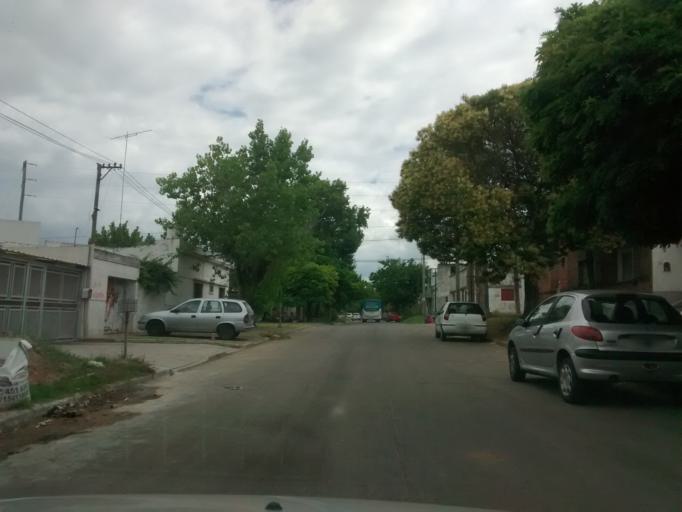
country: AR
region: Buenos Aires
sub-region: Partido de La Plata
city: La Plata
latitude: -34.9352
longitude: -57.9283
